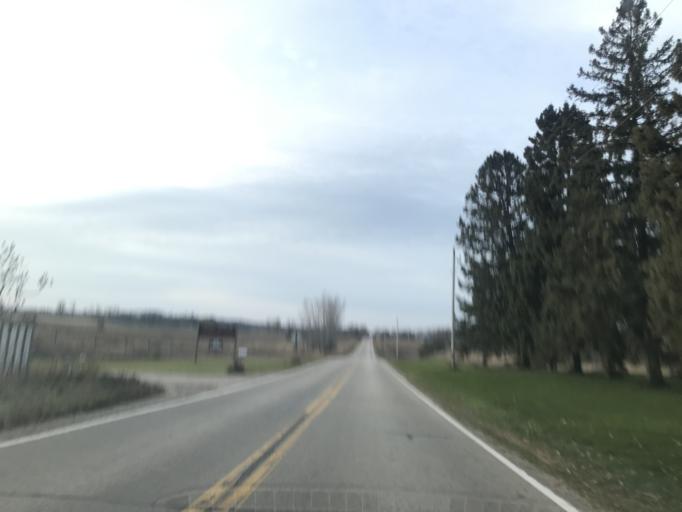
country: US
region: Wisconsin
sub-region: Marinette County
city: Peshtigo
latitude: 45.0990
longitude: -87.7994
